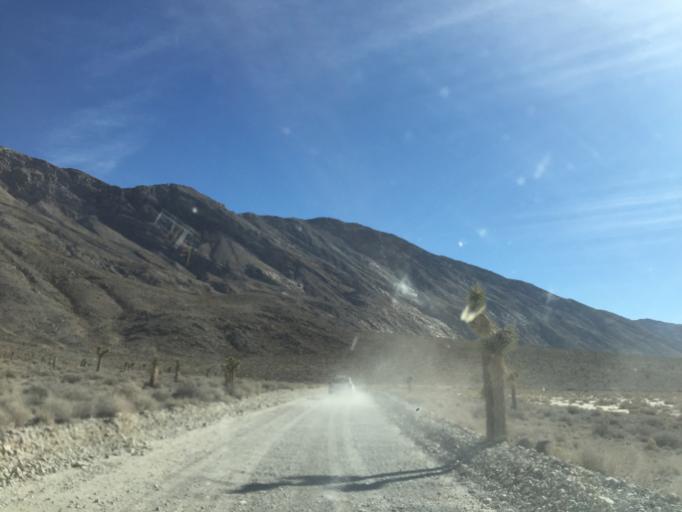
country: US
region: California
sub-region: Inyo County
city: Lone Pine
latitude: 36.8529
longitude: -117.4983
